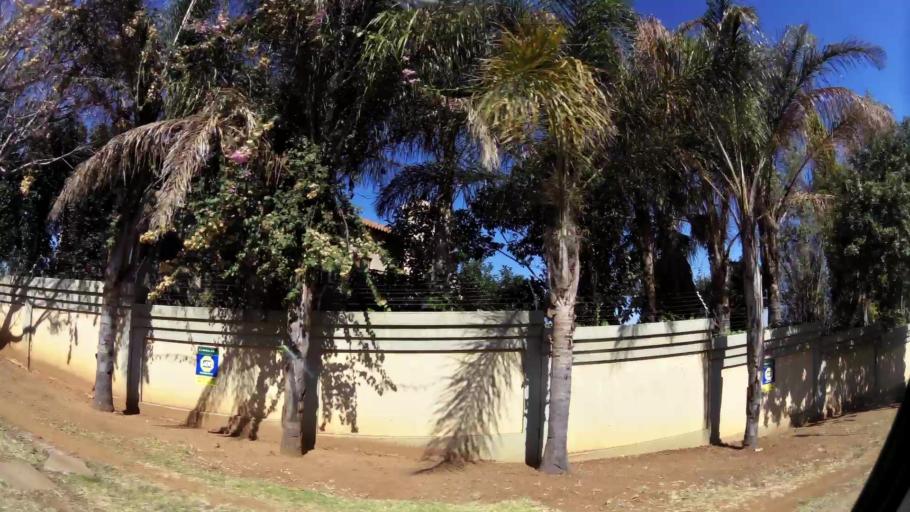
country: ZA
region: Gauteng
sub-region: City of Tshwane Metropolitan Municipality
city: Centurion
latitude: -25.8031
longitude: 28.2409
